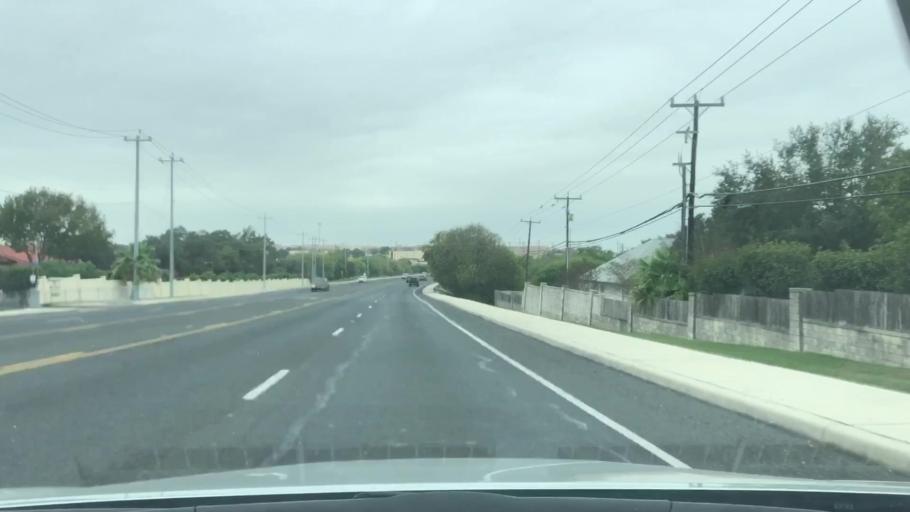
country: US
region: Texas
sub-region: Bexar County
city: Converse
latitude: 29.4879
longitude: -98.3415
